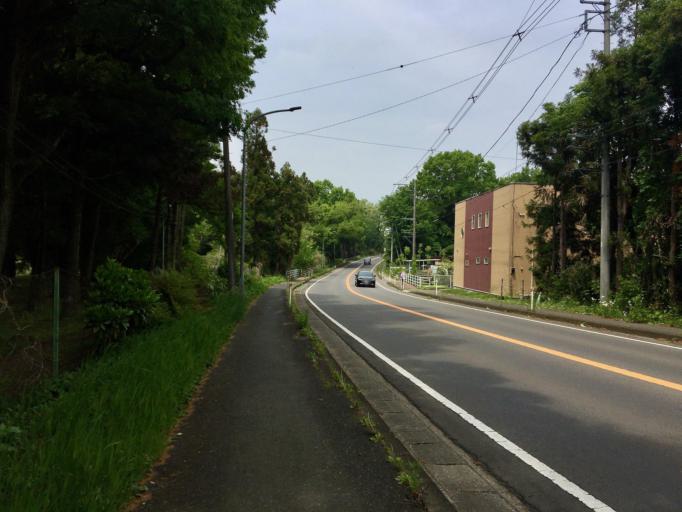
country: JP
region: Tochigi
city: Oyama
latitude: 36.3437
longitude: 139.8145
